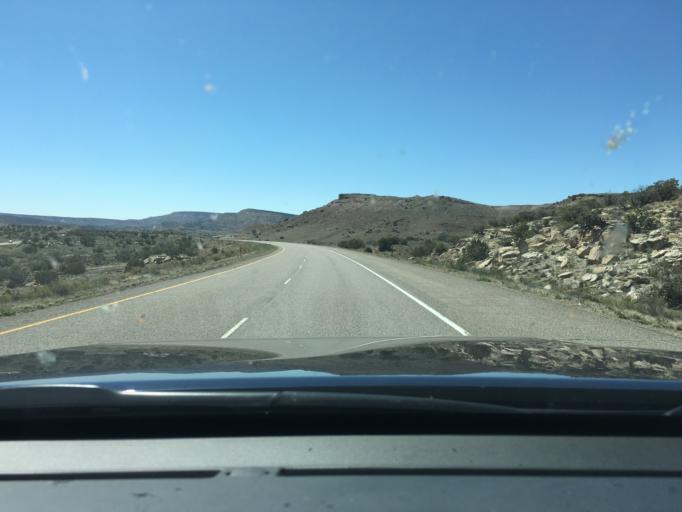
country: US
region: Colorado
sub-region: Mesa County
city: Loma
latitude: 39.2083
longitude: -108.9800
